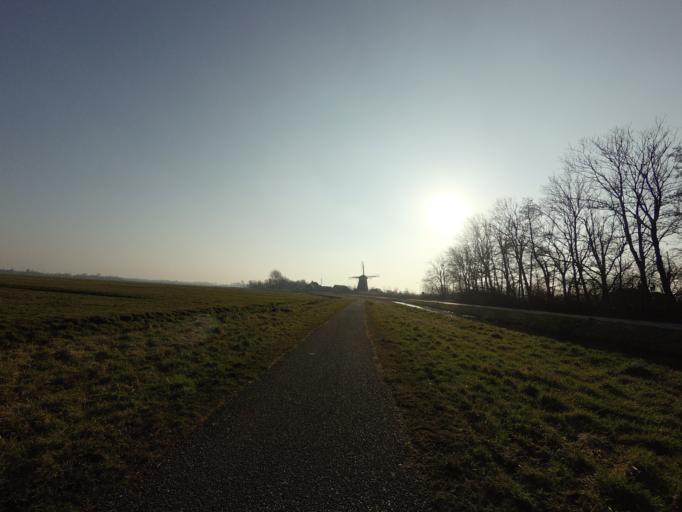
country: NL
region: North Holland
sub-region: Gemeente Haarlem
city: Haarlem
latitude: 52.4091
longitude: 4.6825
